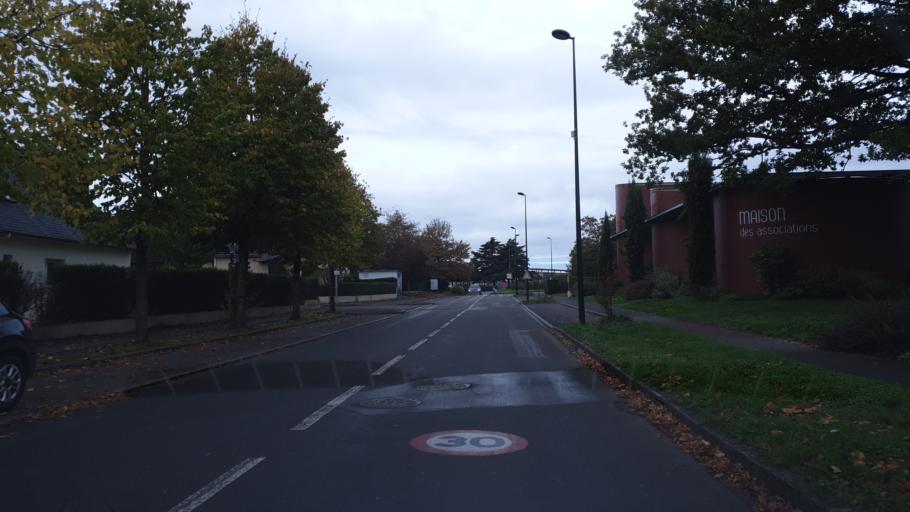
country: FR
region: Brittany
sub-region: Departement d'Ille-et-Vilaine
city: Chartres-de-Bretagne
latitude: 48.0464
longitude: -1.7076
